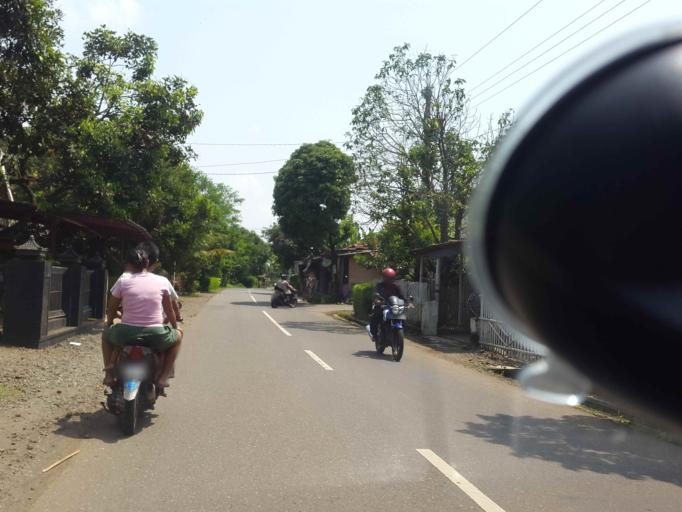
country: ID
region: Central Java
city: Sokaraja
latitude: -7.4695
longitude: 109.2836
